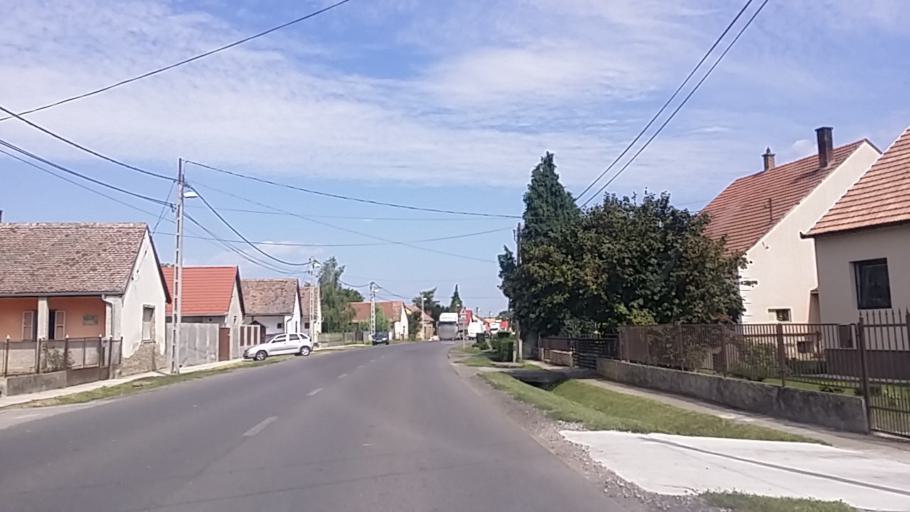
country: HU
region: Tolna
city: Dombovar
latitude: 46.3328
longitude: 18.1272
